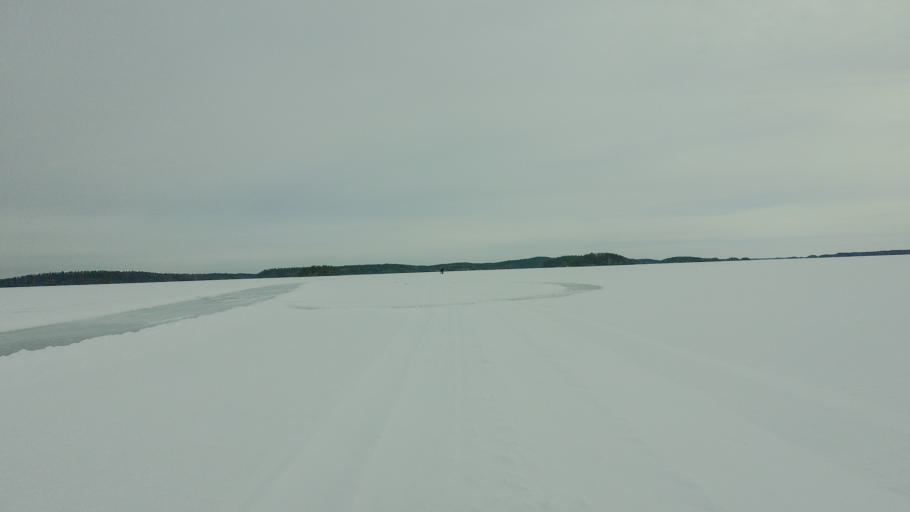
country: FI
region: Southern Savonia
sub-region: Savonlinna
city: Rantasalmi
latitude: 62.1029
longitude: 28.4471
